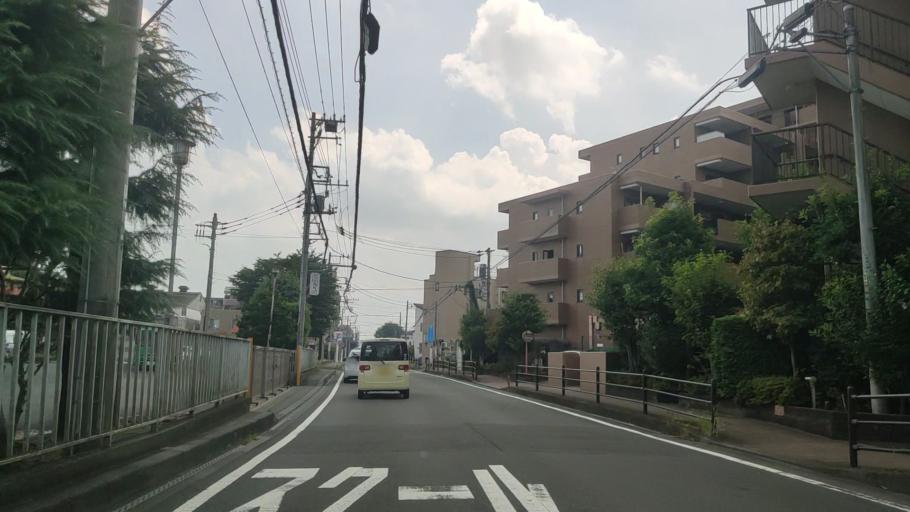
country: JP
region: Tokyo
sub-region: Machida-shi
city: Machida
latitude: 35.5476
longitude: 139.4269
